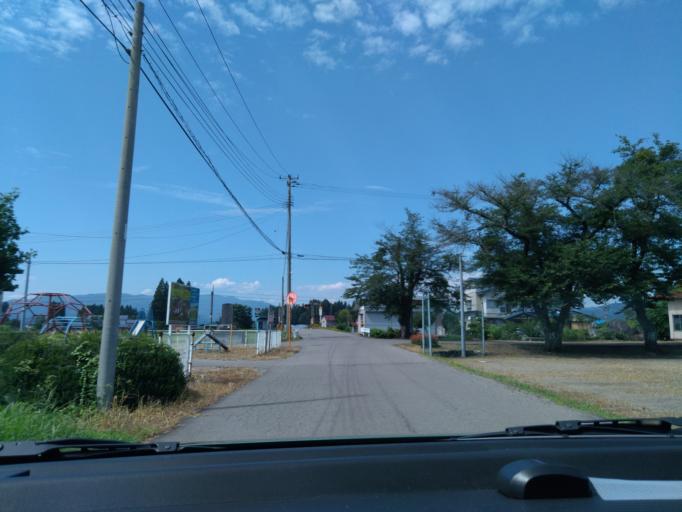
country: JP
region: Akita
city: Kakunodatemachi
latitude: 39.6080
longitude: 140.5950
